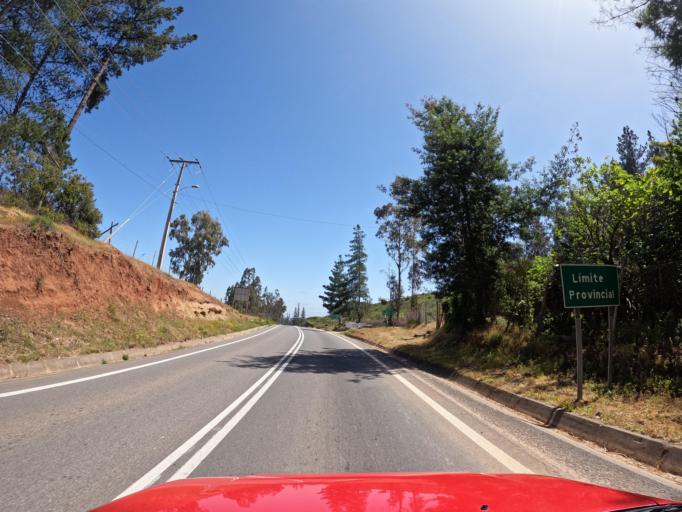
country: CL
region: O'Higgins
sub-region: Provincia de Colchagua
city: Santa Cruz
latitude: -34.6796
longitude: -71.7923
